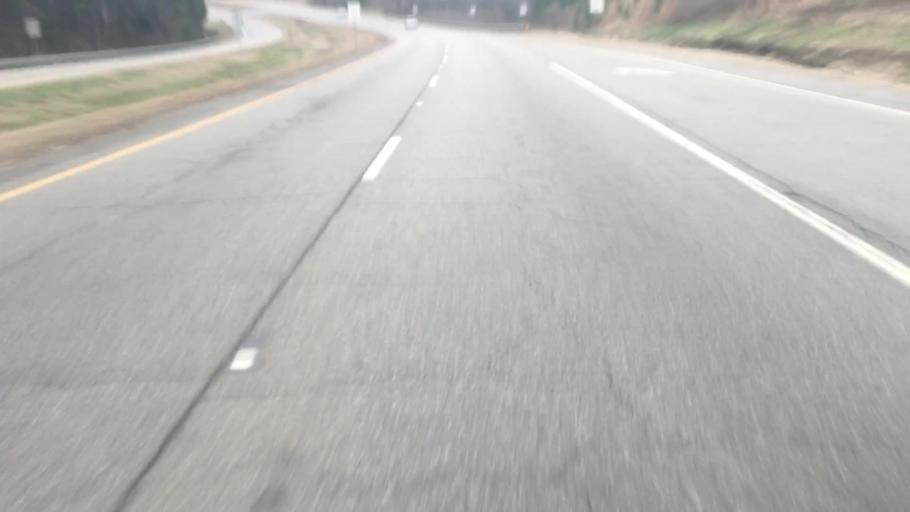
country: US
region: Alabama
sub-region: Walker County
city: Sumiton
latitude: 33.7499
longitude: -87.0579
